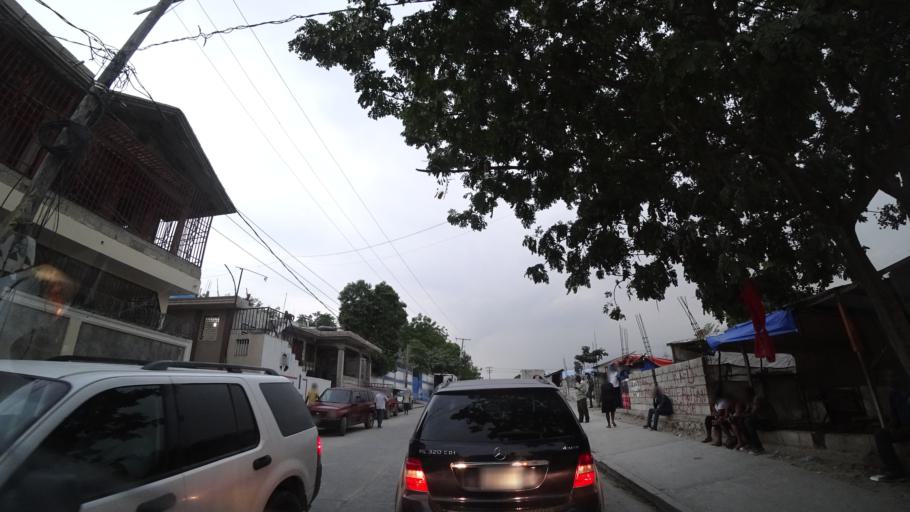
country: HT
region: Ouest
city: Delmas 73
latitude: 18.5614
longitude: -72.2935
